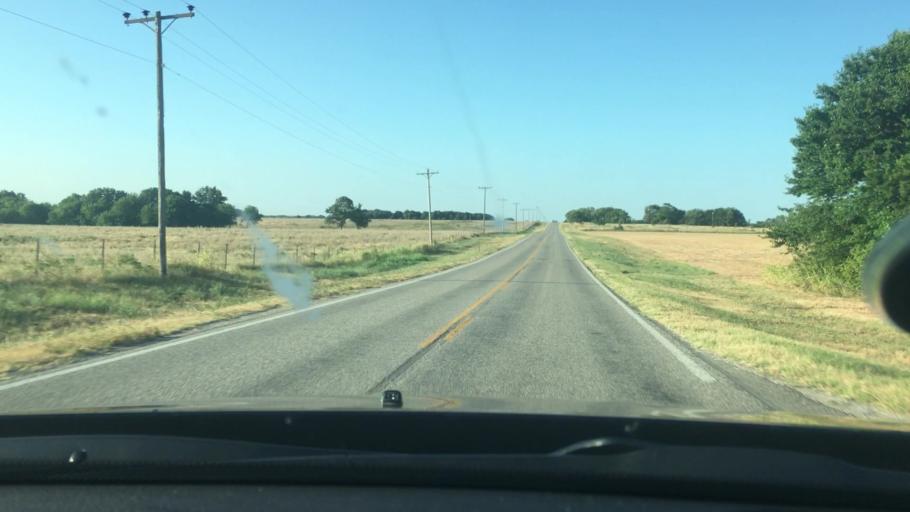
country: US
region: Oklahoma
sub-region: Murray County
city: Sulphur
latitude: 34.5788
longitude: -96.8448
